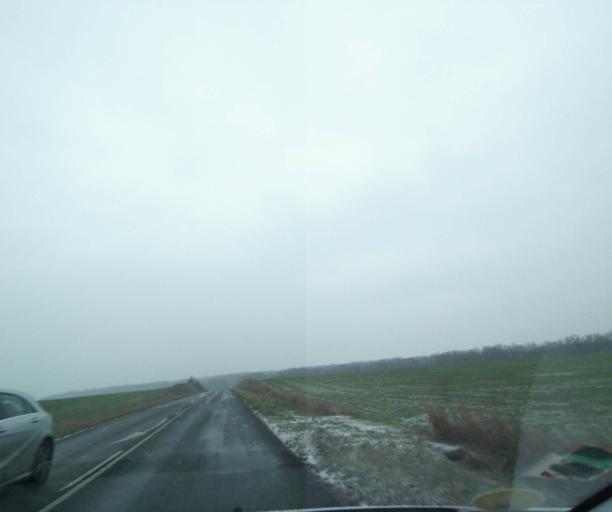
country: FR
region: Champagne-Ardenne
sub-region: Departement de la Haute-Marne
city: Wassy
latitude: 48.4792
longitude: 5.0063
